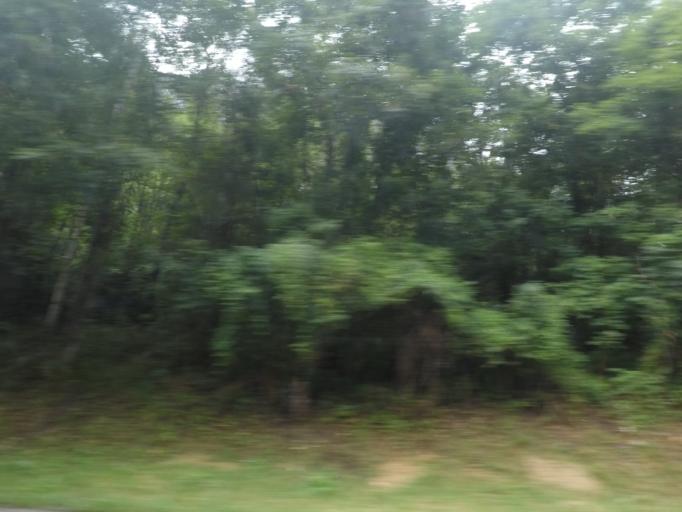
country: IT
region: Aosta Valley
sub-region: Valle d'Aosta
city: Antey-Saint-Andre
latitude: 45.8232
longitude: 7.5900
